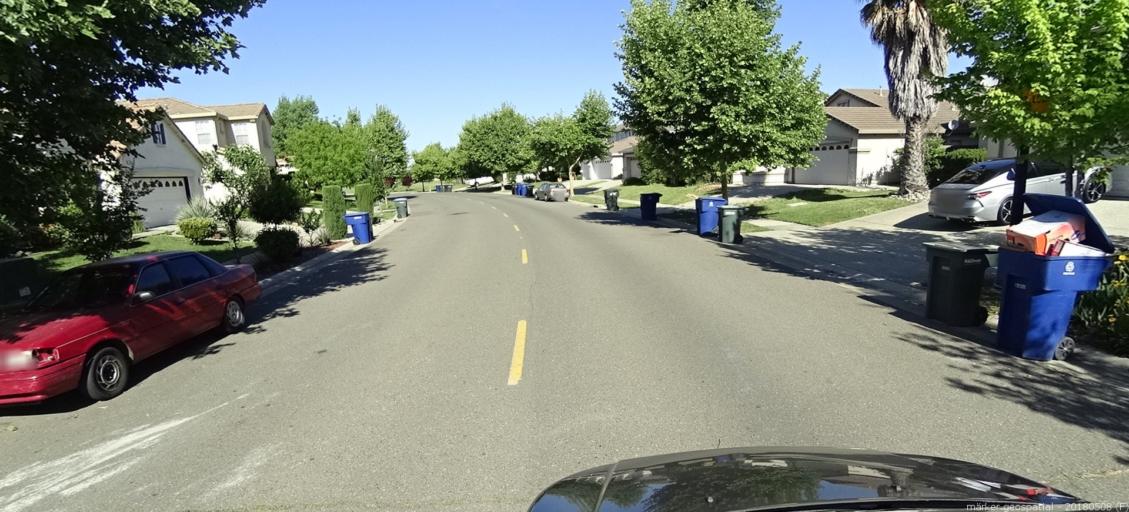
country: US
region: California
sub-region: Sacramento County
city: Rio Linda
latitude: 38.6760
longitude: -121.4970
